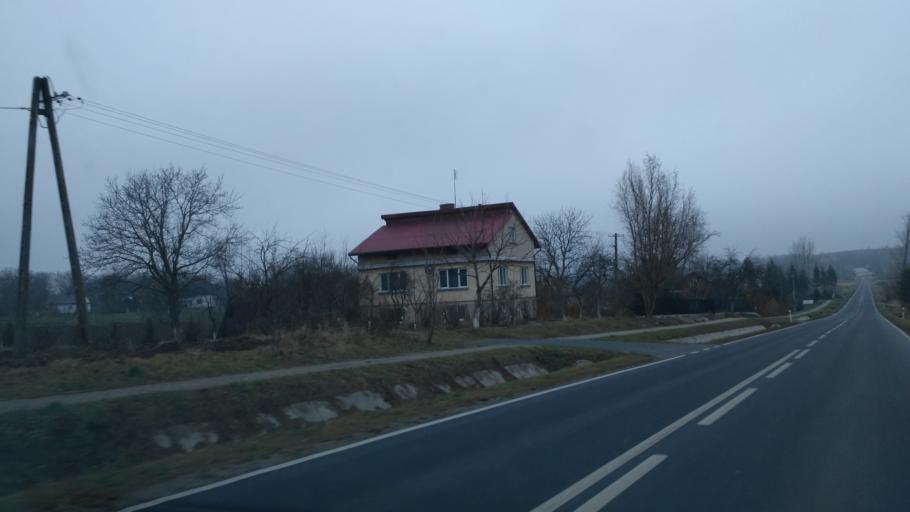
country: PL
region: Subcarpathian Voivodeship
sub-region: Powiat jaroslawski
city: Pruchnik
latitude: 49.9221
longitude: 22.5676
